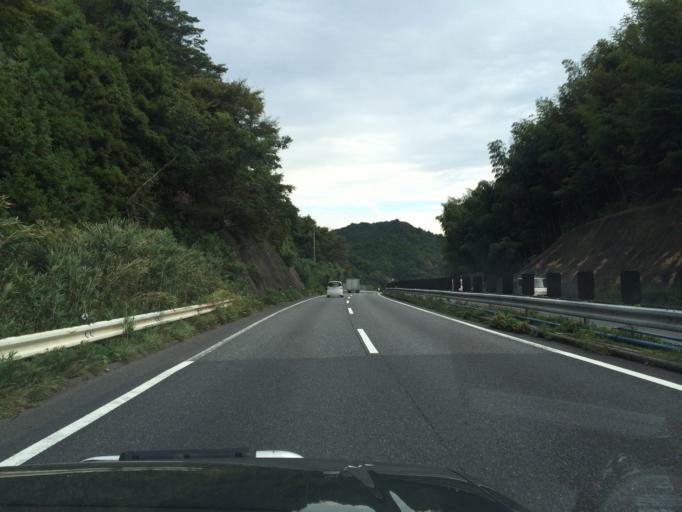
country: JP
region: Mie
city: Kameyama
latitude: 34.8416
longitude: 136.3691
